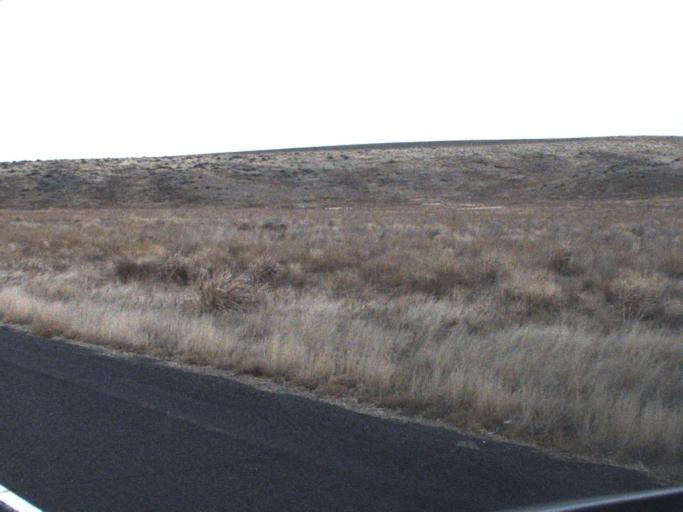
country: US
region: Washington
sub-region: Garfield County
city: Pomeroy
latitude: 46.7976
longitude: -117.8647
